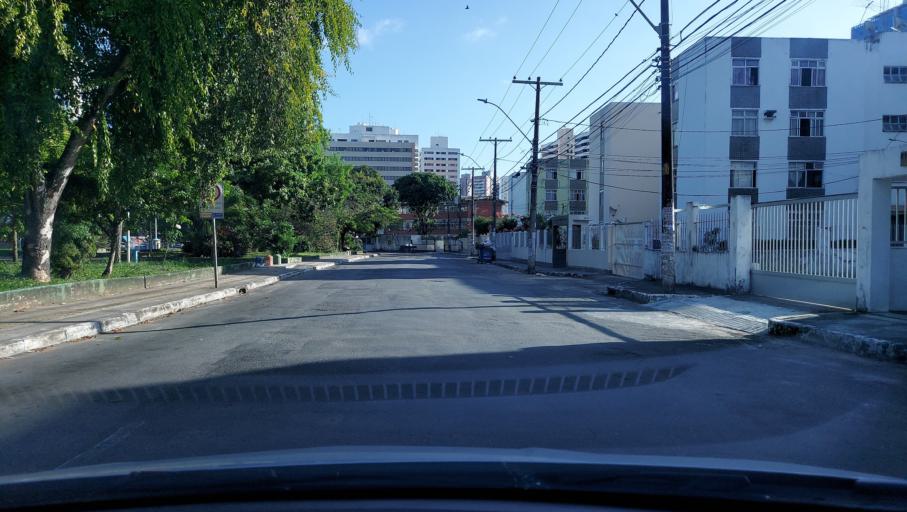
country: BR
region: Bahia
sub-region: Salvador
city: Salvador
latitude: -12.9787
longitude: -38.4481
